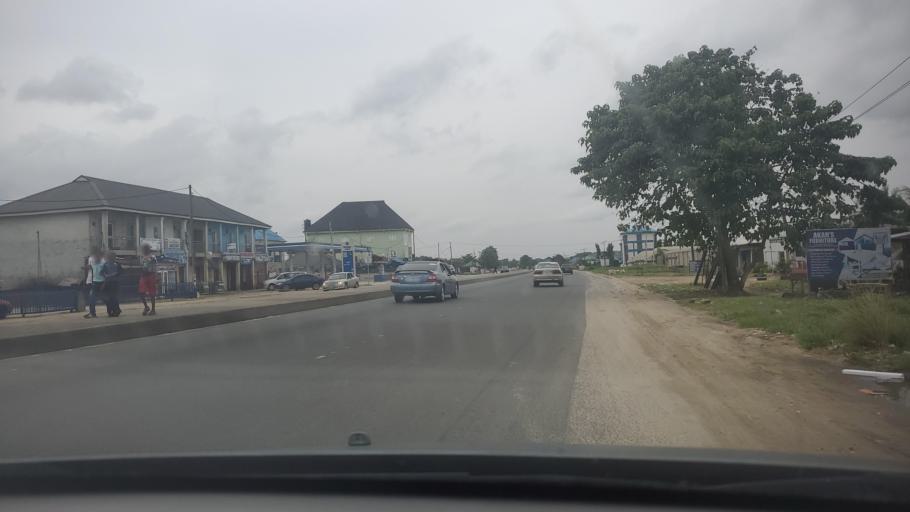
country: NG
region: Rivers
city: Emuoha
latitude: 4.8725
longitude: 6.9615
